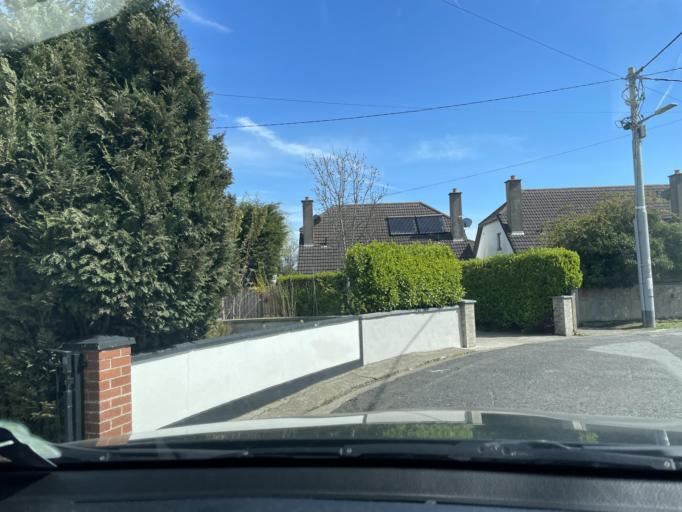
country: IE
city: Killester
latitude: 53.3776
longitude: -6.2009
